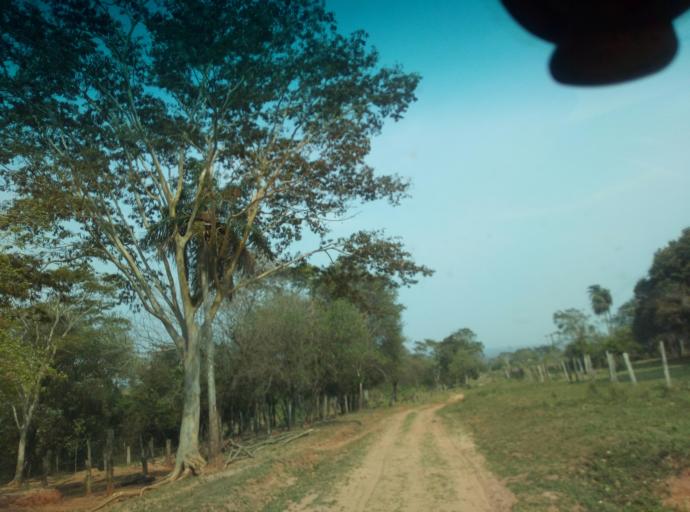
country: PY
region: Caaguazu
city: San Joaquin
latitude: -25.1426
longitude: -56.1014
